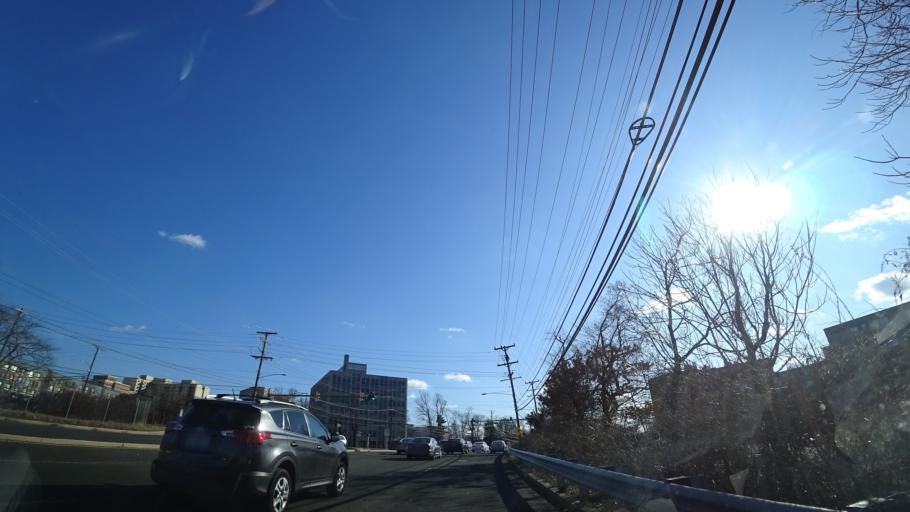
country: US
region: Maryland
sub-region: Montgomery County
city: Silver Spring
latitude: 38.9970
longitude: -77.0370
